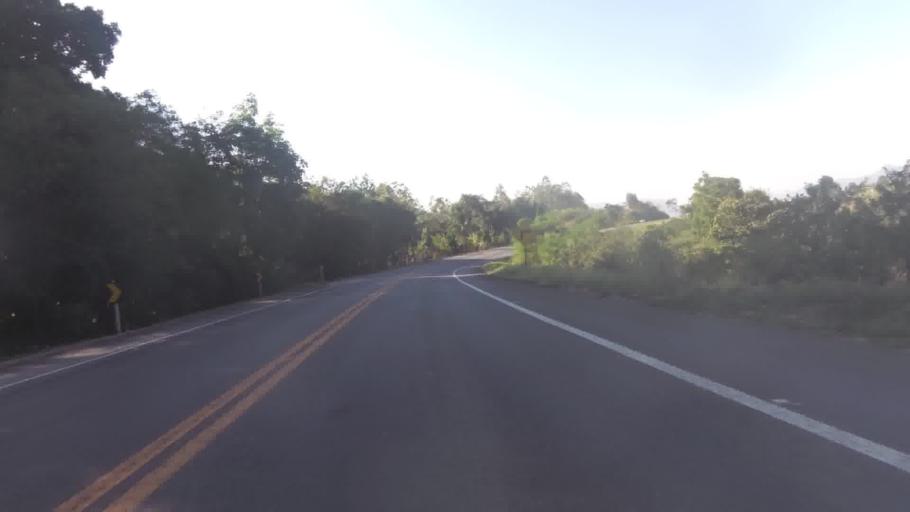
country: BR
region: Espirito Santo
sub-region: Alfredo Chaves
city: Alfredo Chaves
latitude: -20.7067
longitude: -40.7181
